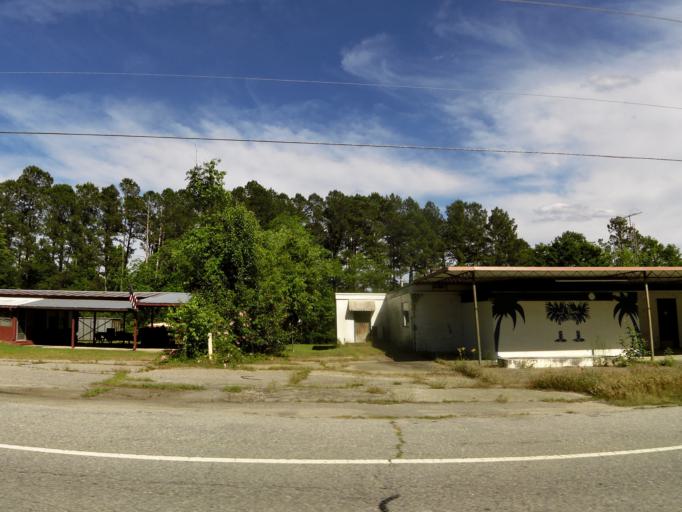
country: US
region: South Carolina
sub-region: Bamberg County
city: Denmark
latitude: 33.1870
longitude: -81.1828
